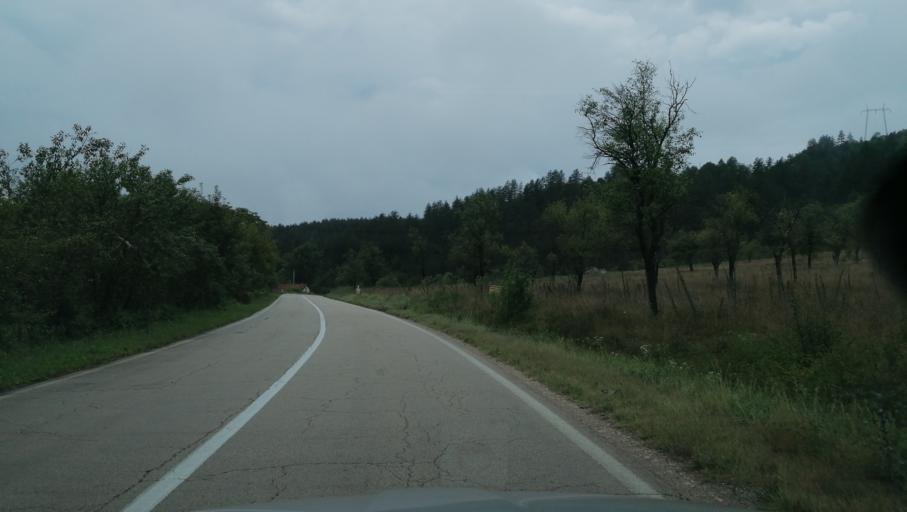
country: BA
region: Republika Srpska
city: Visegrad
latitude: 43.7876
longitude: 19.3303
